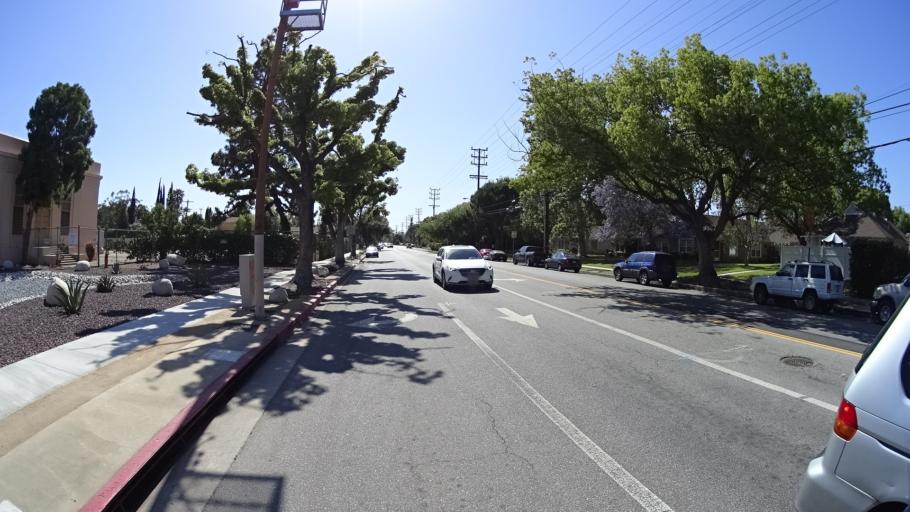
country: US
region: California
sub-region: Los Angeles County
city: Universal City
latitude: 34.1576
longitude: -118.3618
